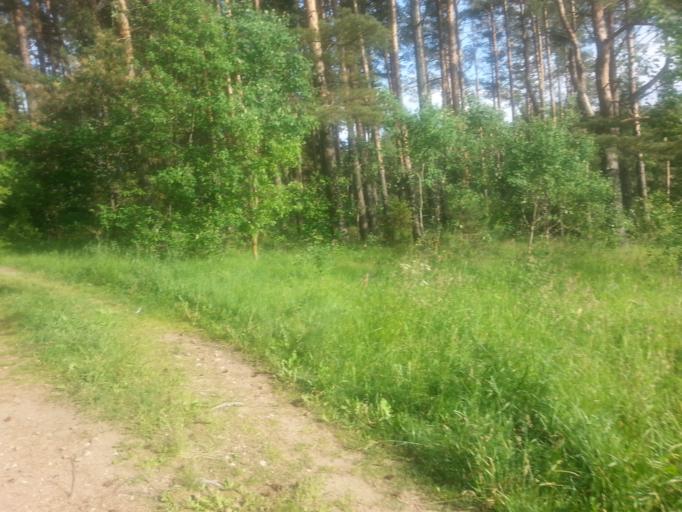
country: BY
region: Minsk
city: Narach
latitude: 54.9683
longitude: 26.6158
